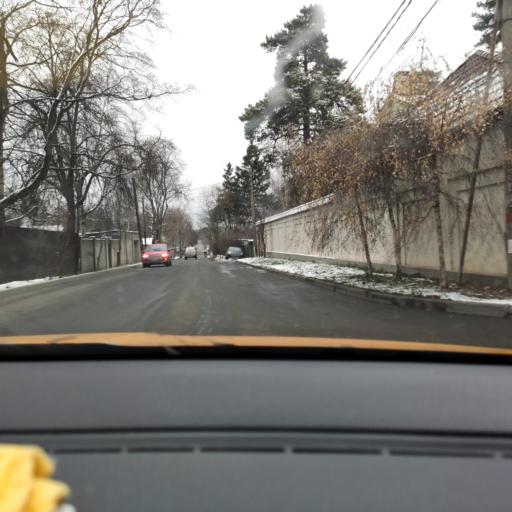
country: RU
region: Moskovskaya
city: Druzhba
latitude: 55.8880
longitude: 37.7461
